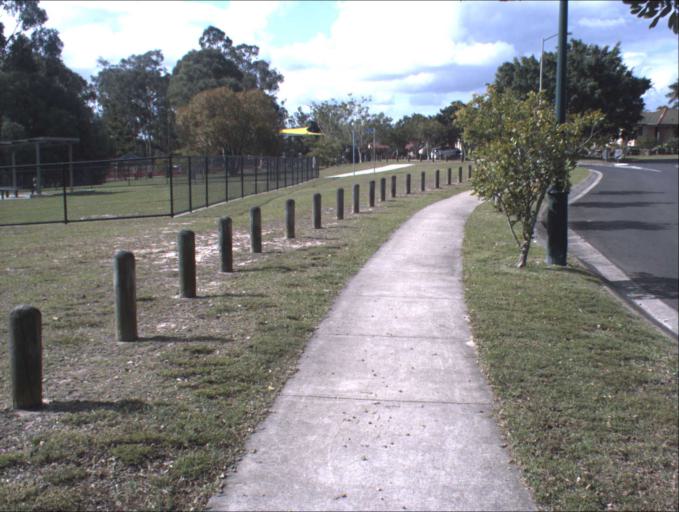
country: AU
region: Queensland
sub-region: Logan
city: Park Ridge South
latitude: -27.6879
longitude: 153.0515
